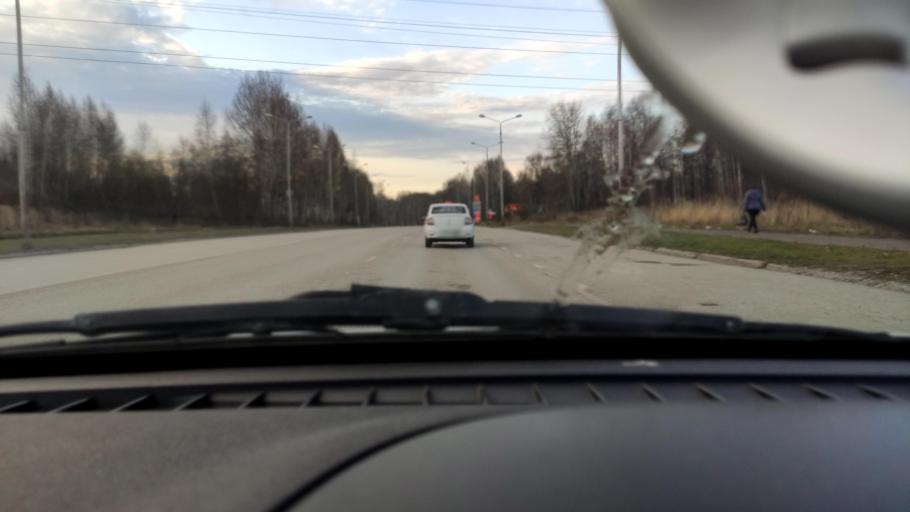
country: RU
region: Perm
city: Perm
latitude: 58.1003
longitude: 56.3885
